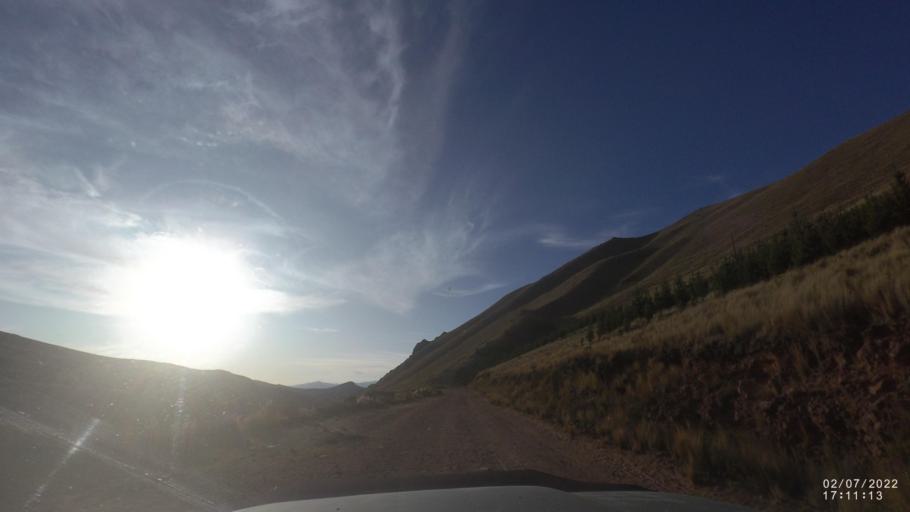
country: BO
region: Cochabamba
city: Irpa Irpa
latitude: -17.8914
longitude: -66.5640
